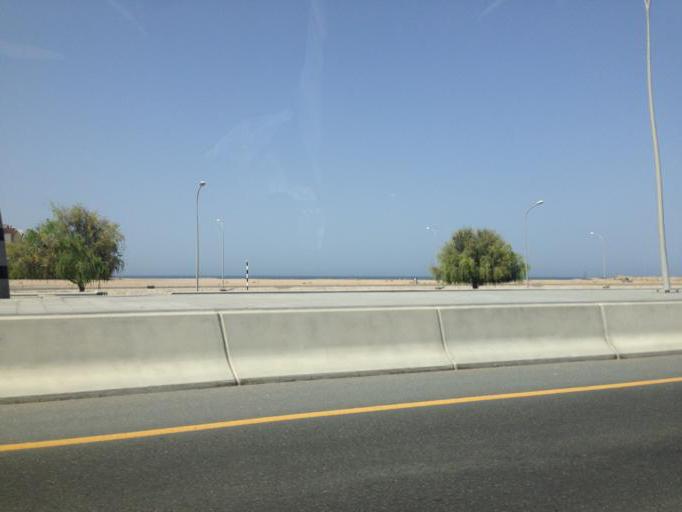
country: OM
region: Muhafazat Masqat
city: Bawshar
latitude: 23.6074
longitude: 58.3153
